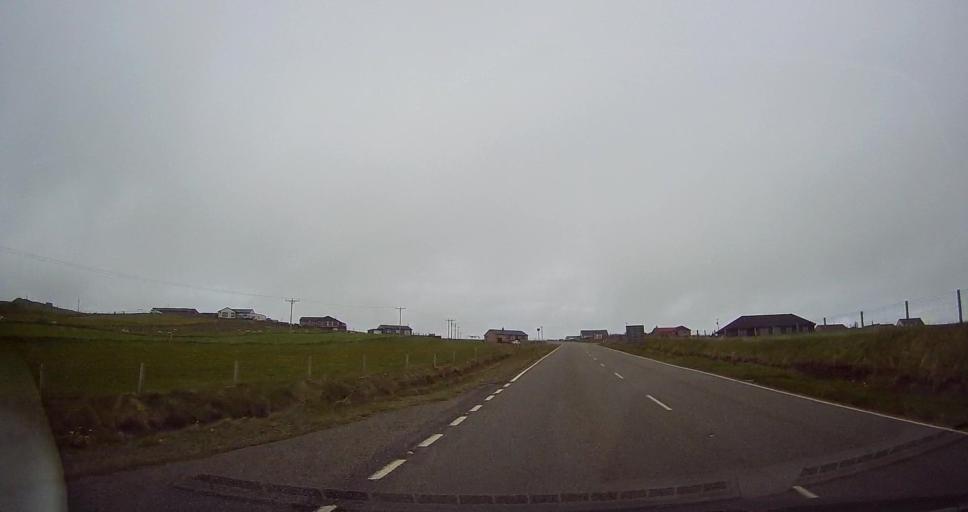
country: GB
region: Scotland
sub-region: Shetland Islands
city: Sandwick
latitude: 59.8923
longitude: -1.3031
